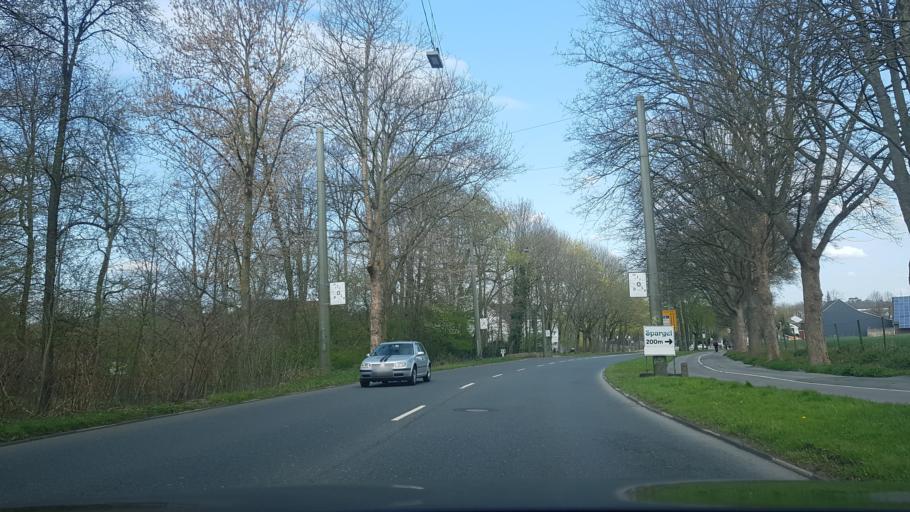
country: DE
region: North Rhine-Westphalia
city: Bochum-Hordel
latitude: 51.4665
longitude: 7.1479
